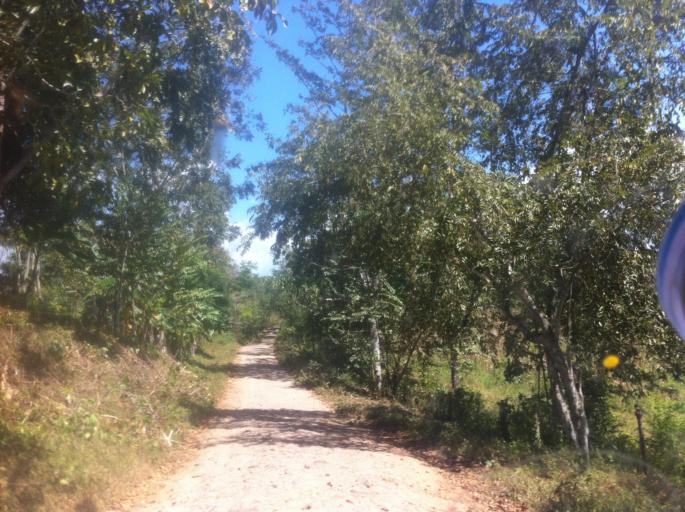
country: NI
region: Rio San Juan
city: San Carlos
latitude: 11.2378
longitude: -84.5238
